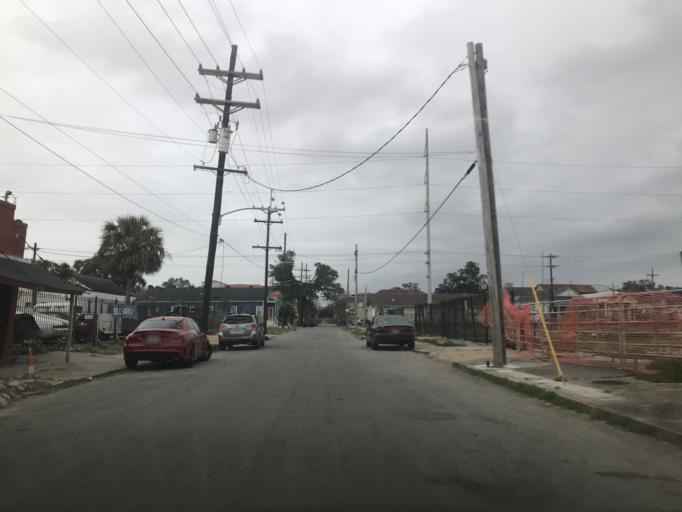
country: US
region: Louisiana
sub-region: Orleans Parish
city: New Orleans
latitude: 29.9645
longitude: -90.0957
